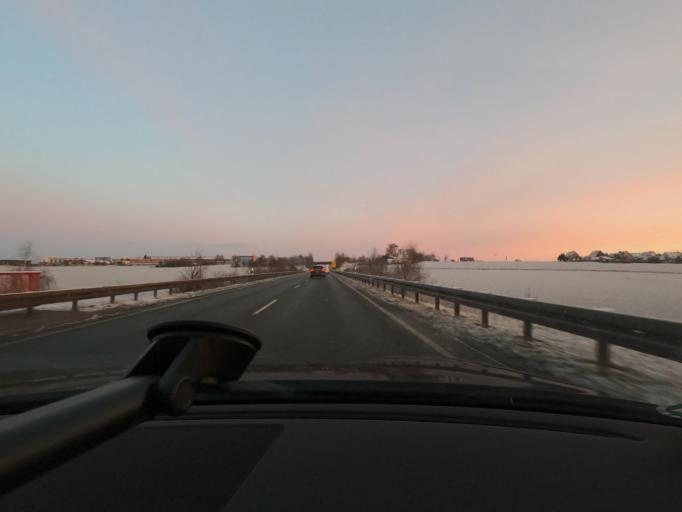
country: DE
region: Thuringia
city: Hausen
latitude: 51.3845
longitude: 10.3467
